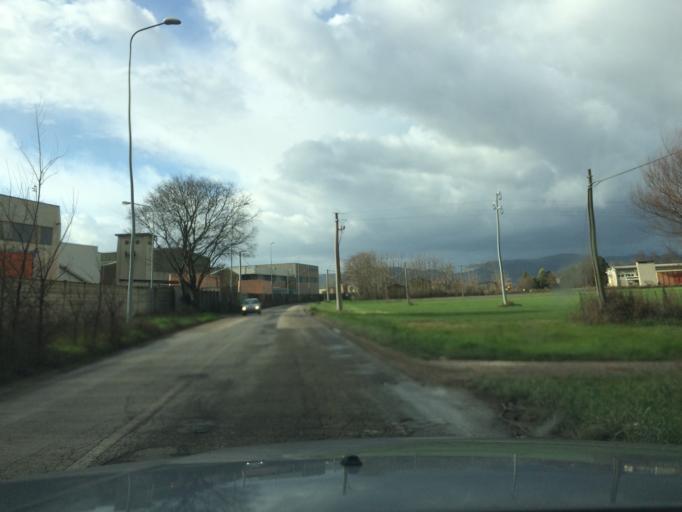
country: IT
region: Umbria
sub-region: Provincia di Terni
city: Terni
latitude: 42.5514
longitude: 12.5894
